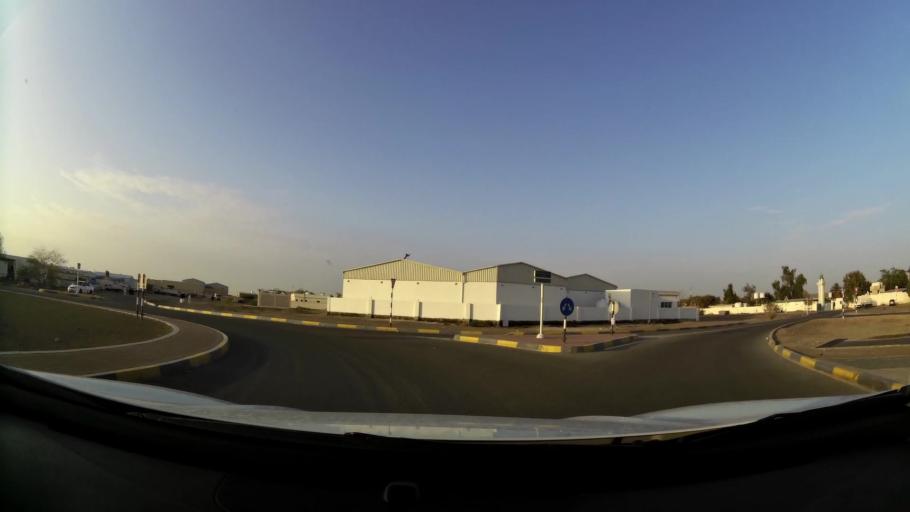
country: AE
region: Abu Dhabi
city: Al Ain
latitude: 24.1540
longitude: 55.8119
